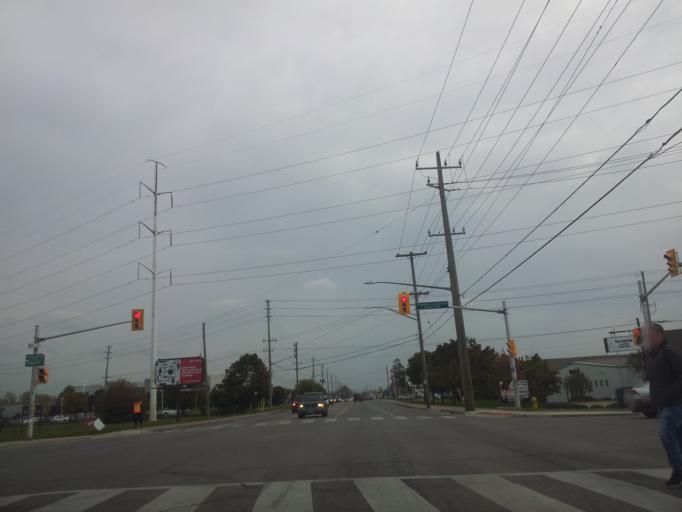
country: CA
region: Ontario
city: London
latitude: 43.0122
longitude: -81.1957
